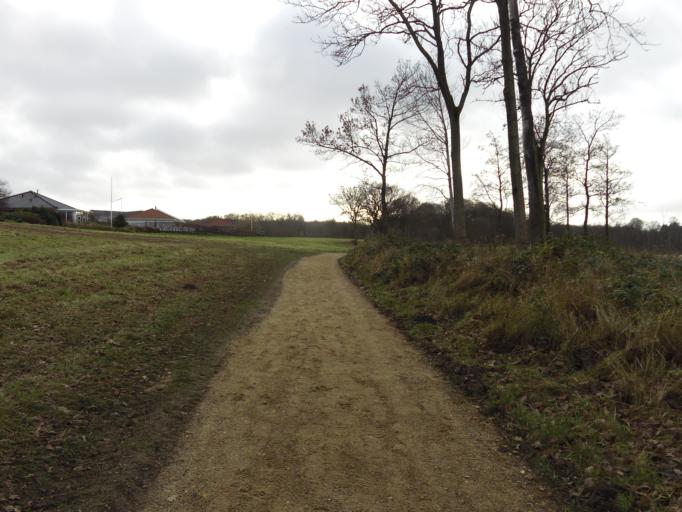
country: DK
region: South Denmark
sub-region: Aabenraa Kommune
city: Krusa
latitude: 54.9300
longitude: 9.4411
